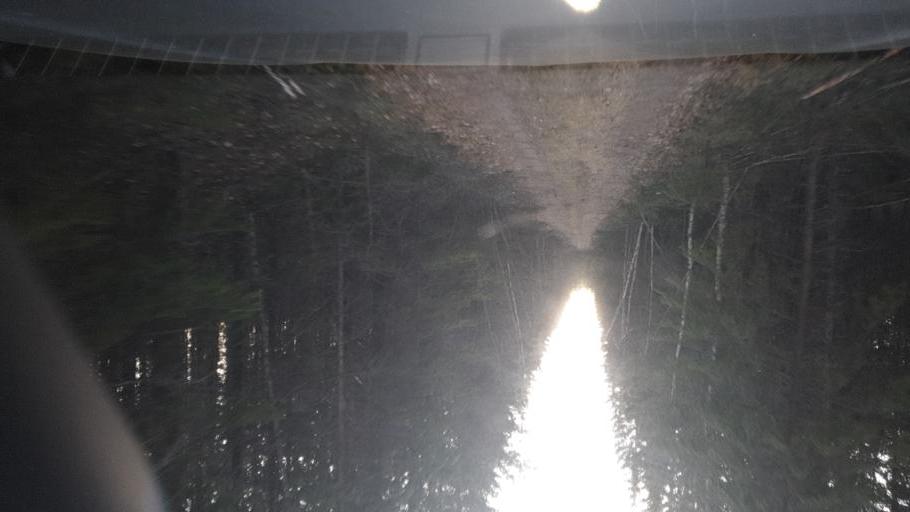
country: SE
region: Vaesternorrland
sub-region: Ange Kommun
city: Ange
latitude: 62.1874
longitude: 15.6127
